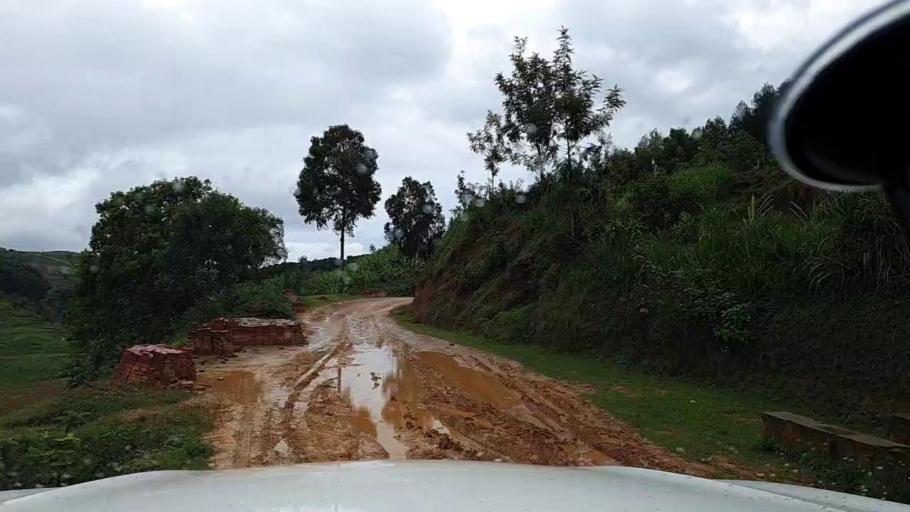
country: RW
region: Western Province
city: Kibuye
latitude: -2.1141
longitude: 29.4910
